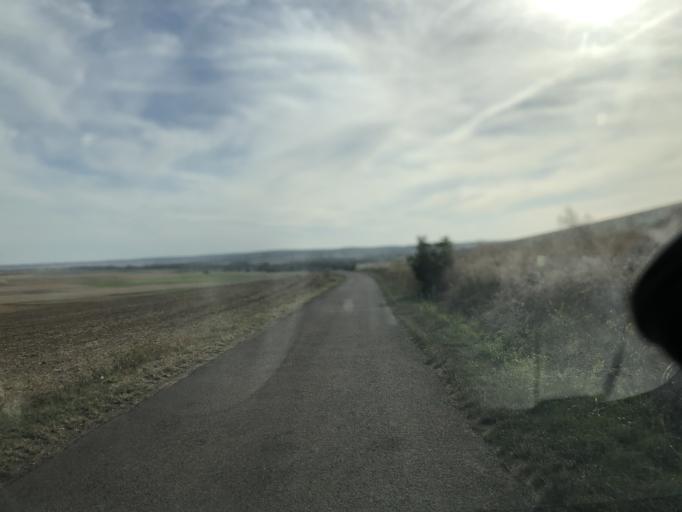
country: FR
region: Bourgogne
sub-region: Departement de l'Yonne
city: Joigny
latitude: 47.9330
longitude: 3.3859
